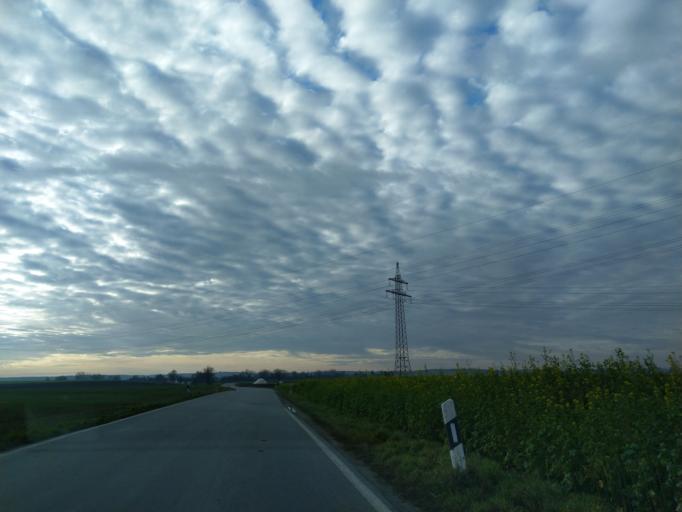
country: DE
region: Bavaria
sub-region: Lower Bavaria
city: Aholming
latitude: 48.7275
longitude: 12.9030
